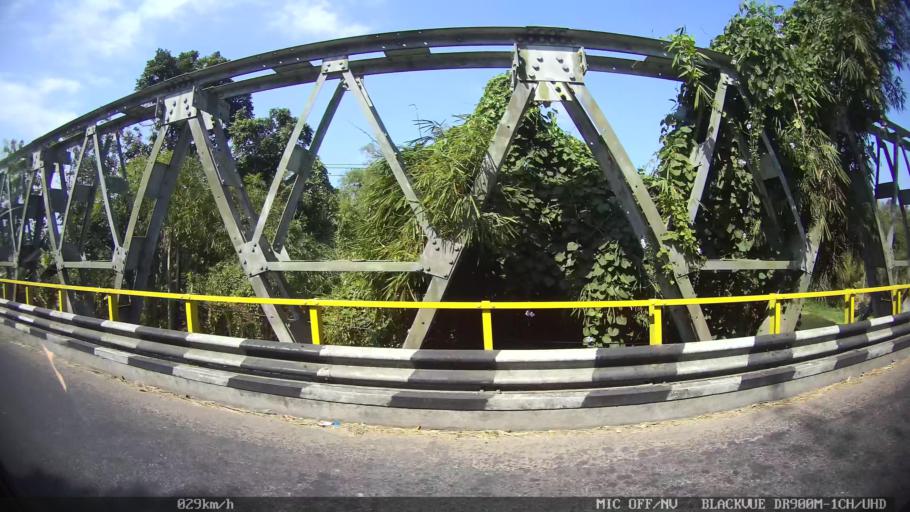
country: ID
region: Daerah Istimewa Yogyakarta
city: Sewon
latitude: -7.9035
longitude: 110.3839
